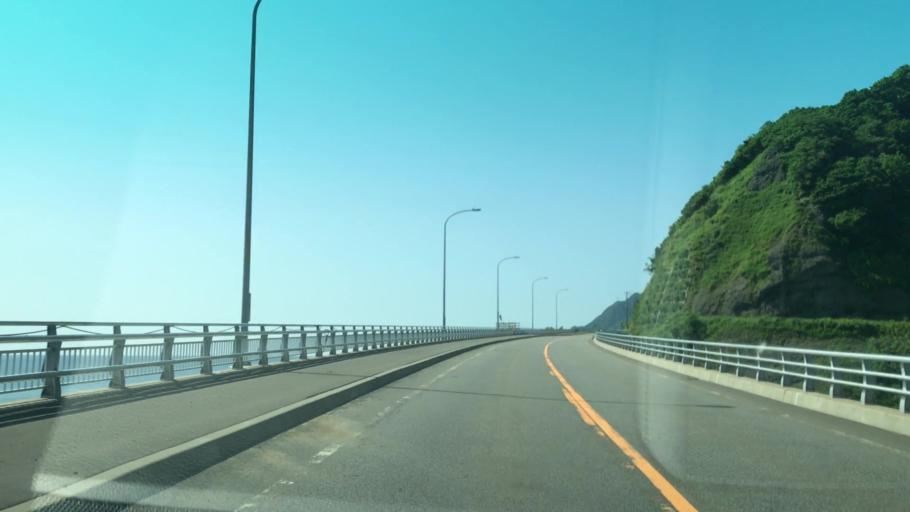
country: JP
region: Hokkaido
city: Iwanai
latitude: 43.1301
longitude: 140.4368
